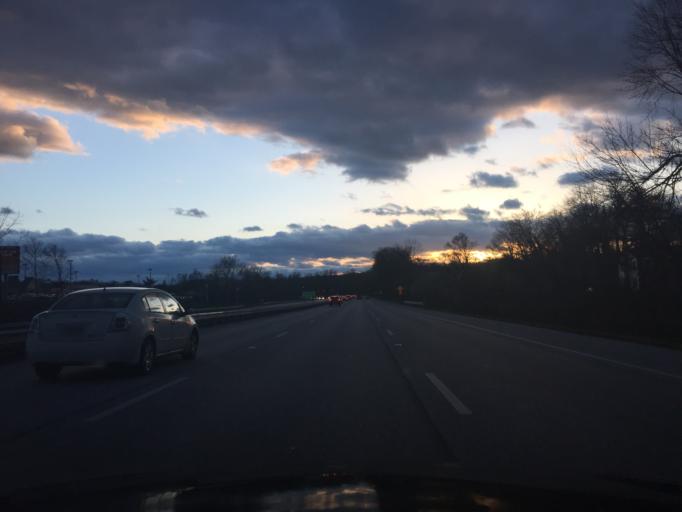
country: US
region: Maryland
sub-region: Baltimore County
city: Parkville
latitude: 39.3743
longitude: -76.5622
